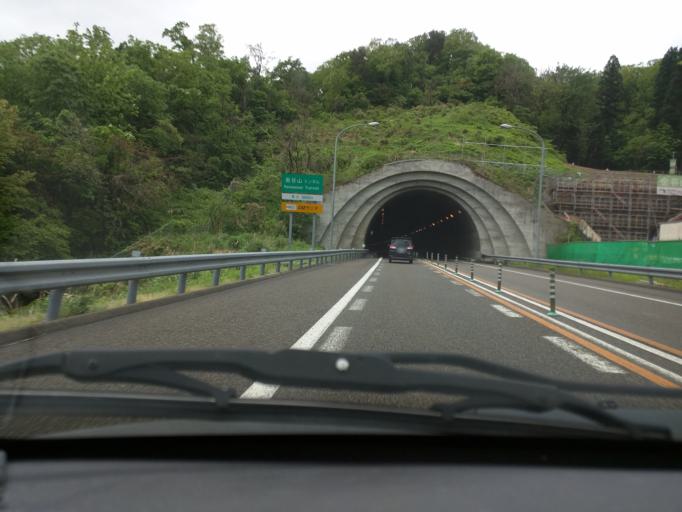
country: JP
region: Niigata
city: Joetsu
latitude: 37.1065
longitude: 138.2198
